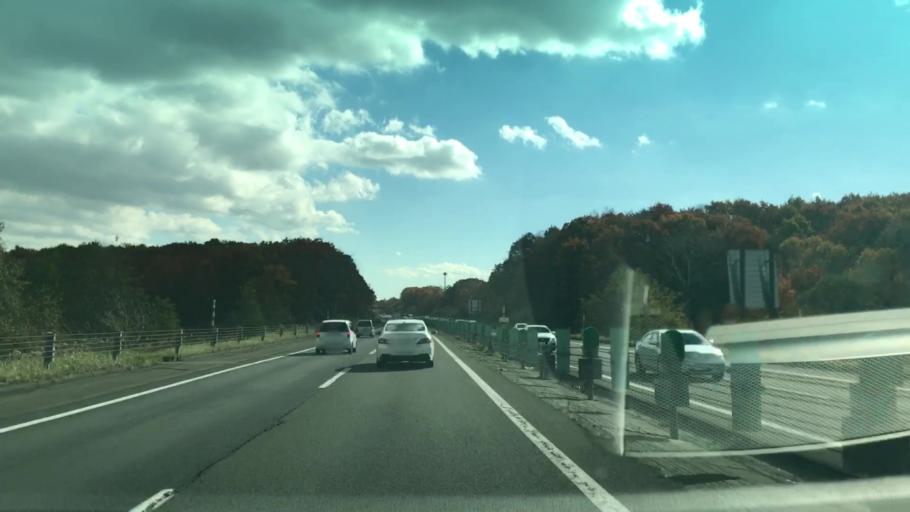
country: JP
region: Hokkaido
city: Kitahiroshima
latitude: 42.9435
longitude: 141.5192
